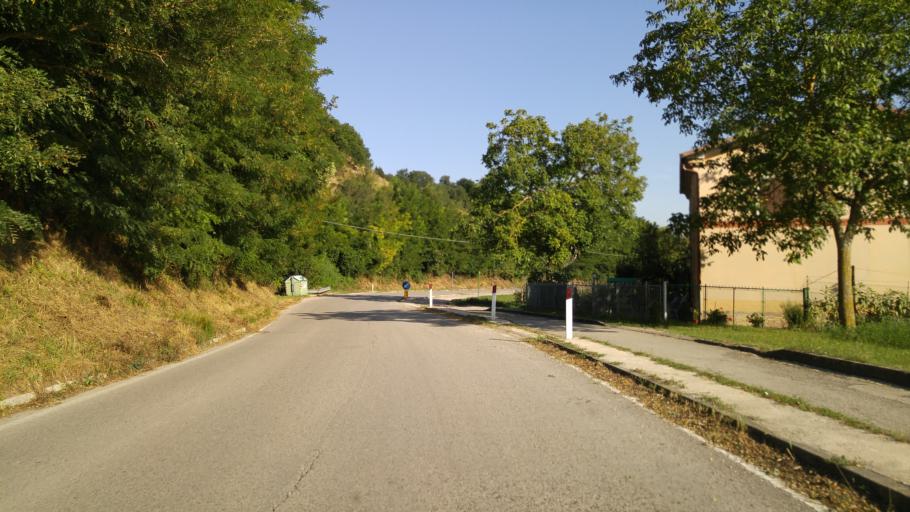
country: IT
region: The Marches
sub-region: Provincia di Pesaro e Urbino
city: Urbania
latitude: 43.6817
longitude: 12.5195
